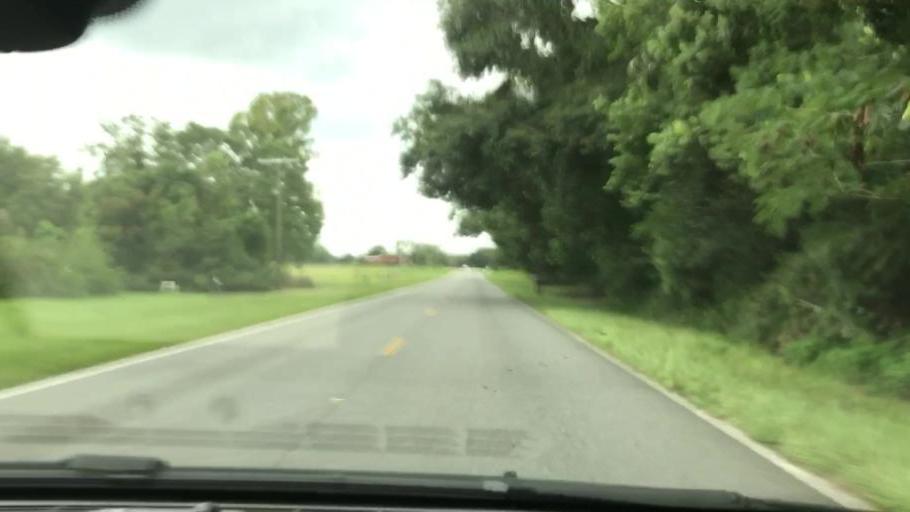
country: US
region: Florida
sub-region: Madison County
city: Madison
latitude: 30.3934
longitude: -83.3004
